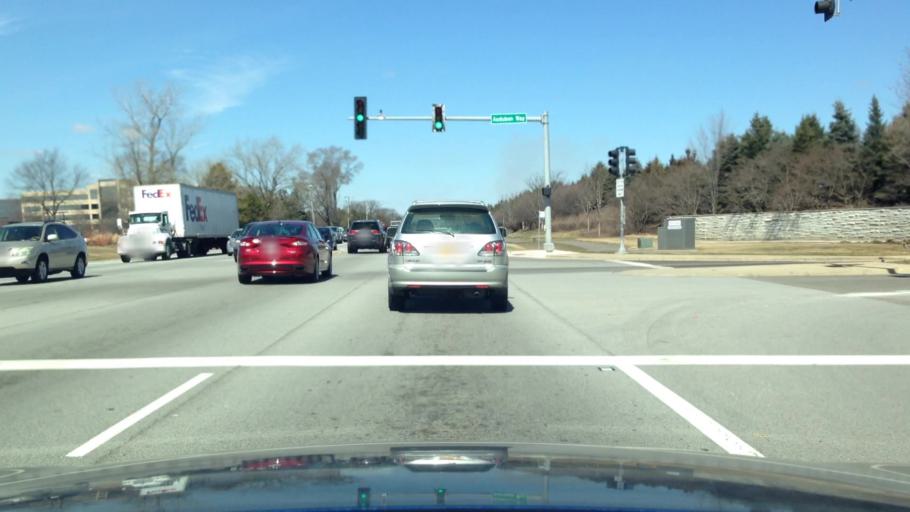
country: US
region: Illinois
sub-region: Lake County
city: Lincolnshire
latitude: 42.1839
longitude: -87.9269
